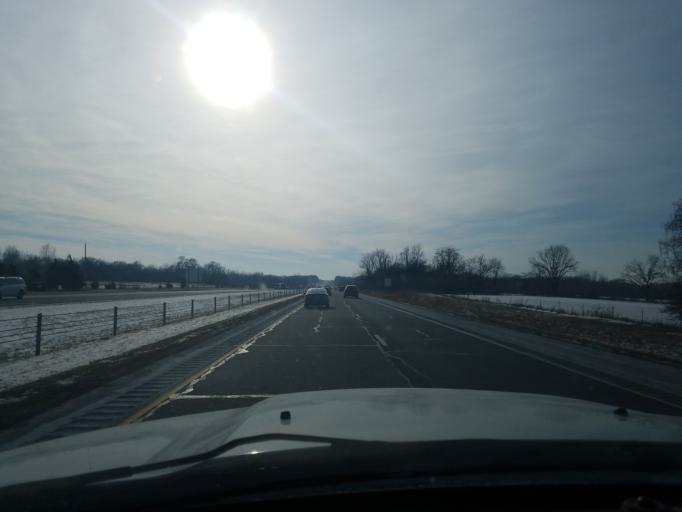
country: US
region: Indiana
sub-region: Huntington County
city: Warren
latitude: 40.7117
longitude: -85.4475
